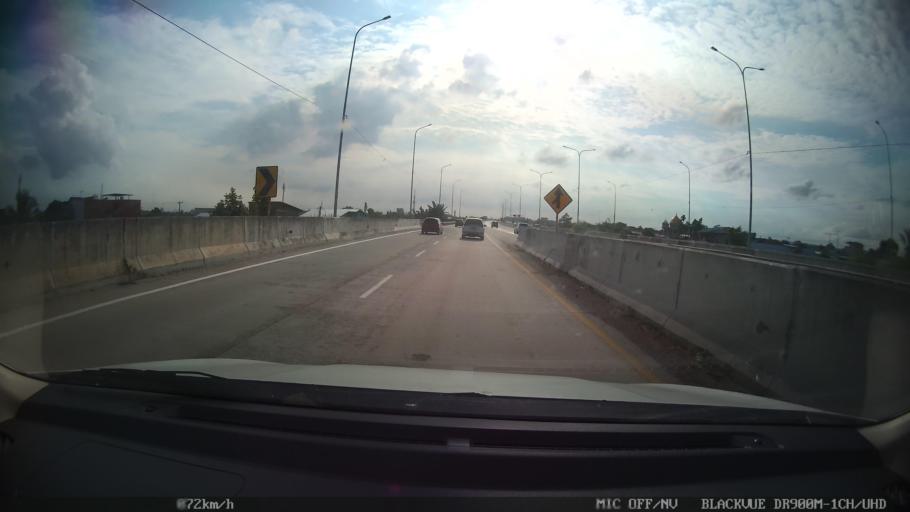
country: ID
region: North Sumatra
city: Medan
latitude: 3.6478
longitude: 98.6753
